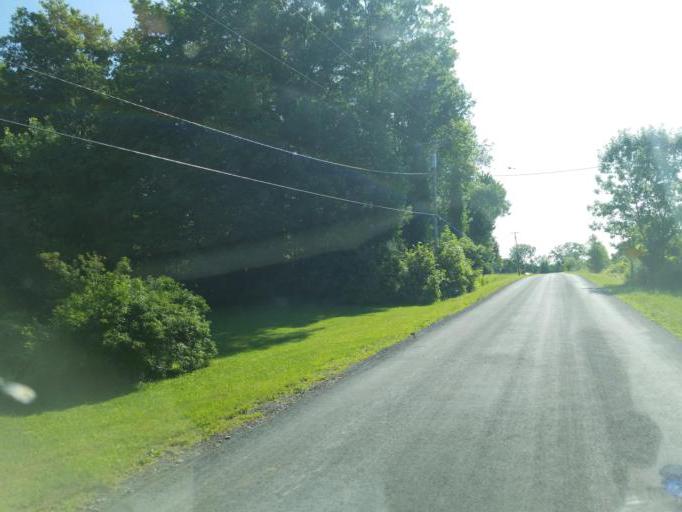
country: US
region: New York
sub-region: Wayne County
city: Clyde
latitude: 43.0438
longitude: -76.8802
